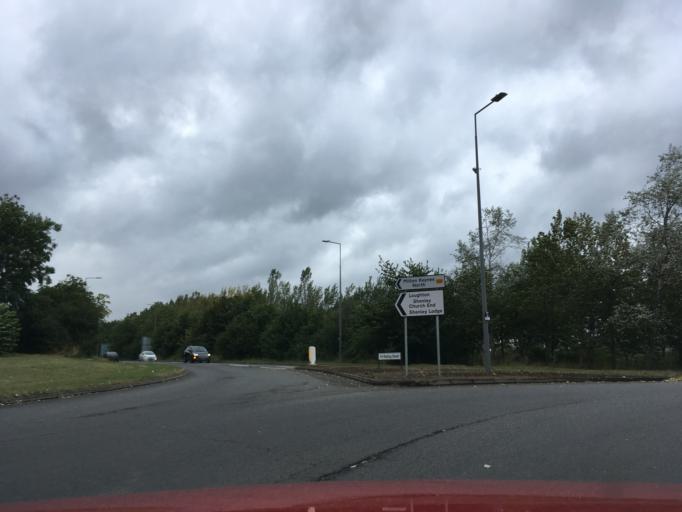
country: GB
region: England
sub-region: Milton Keynes
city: Loughton
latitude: 52.0190
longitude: -0.7680
